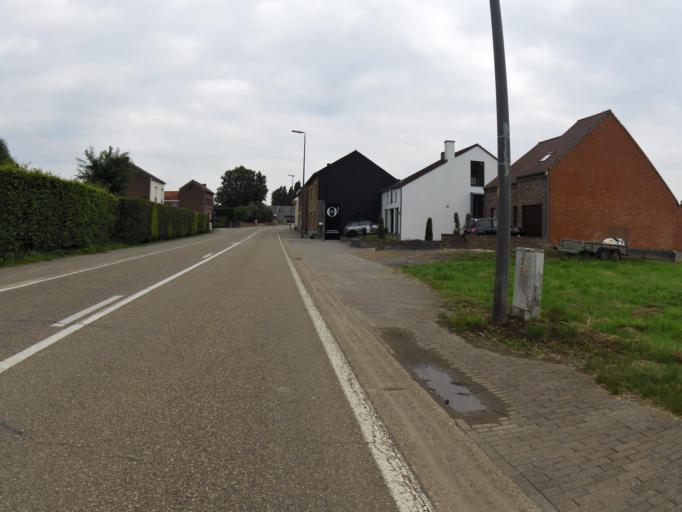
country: BE
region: Flanders
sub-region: Provincie Limburg
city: Tongeren
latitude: 50.7799
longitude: 5.5212
